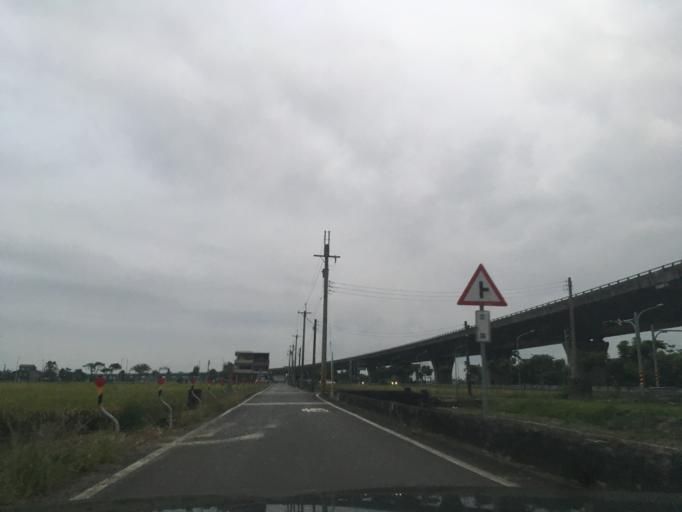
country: TW
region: Taiwan
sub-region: Yilan
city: Yilan
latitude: 24.8184
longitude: 121.7827
